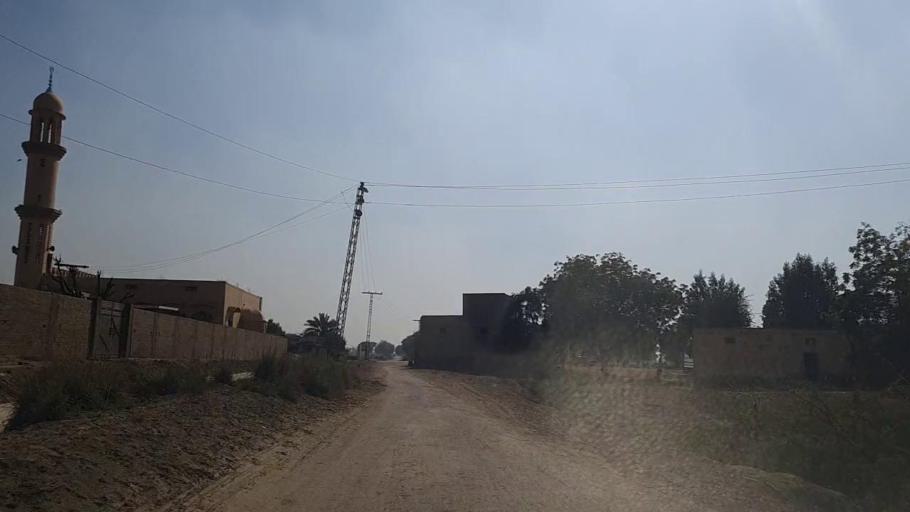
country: PK
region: Sindh
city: Shahpur Chakar
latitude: 26.1892
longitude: 68.5835
